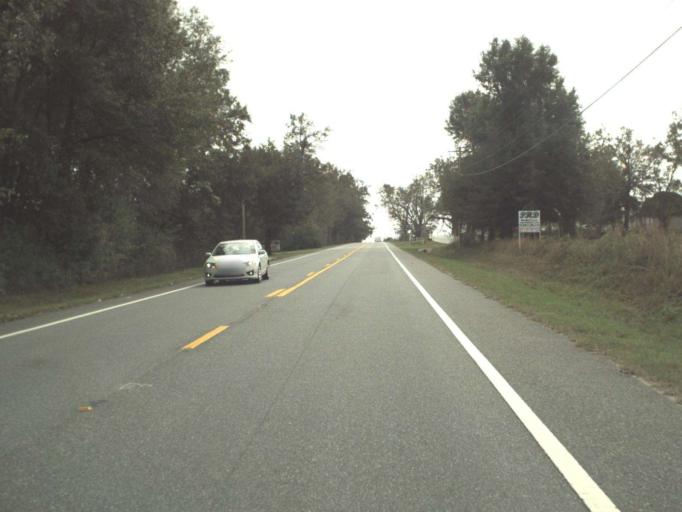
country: US
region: Florida
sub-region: Santa Rosa County
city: Point Baker
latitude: 30.8402
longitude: -87.0504
